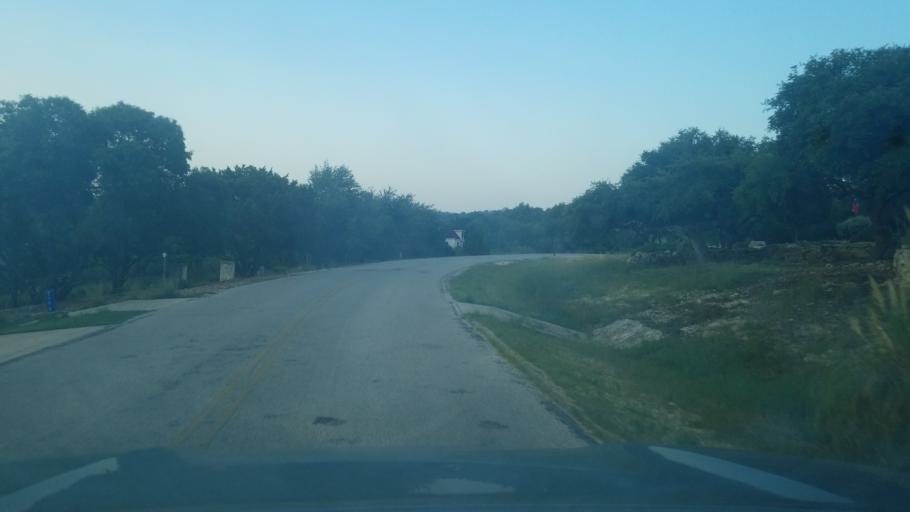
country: US
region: Texas
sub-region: Comal County
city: Bulverde
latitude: 29.8201
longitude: -98.4024
